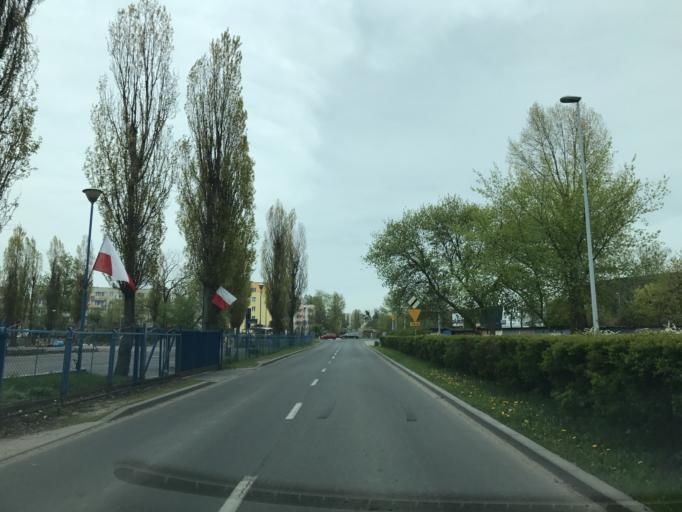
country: PL
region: Kujawsko-Pomorskie
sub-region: Torun
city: Torun
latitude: 53.0178
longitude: 18.5590
